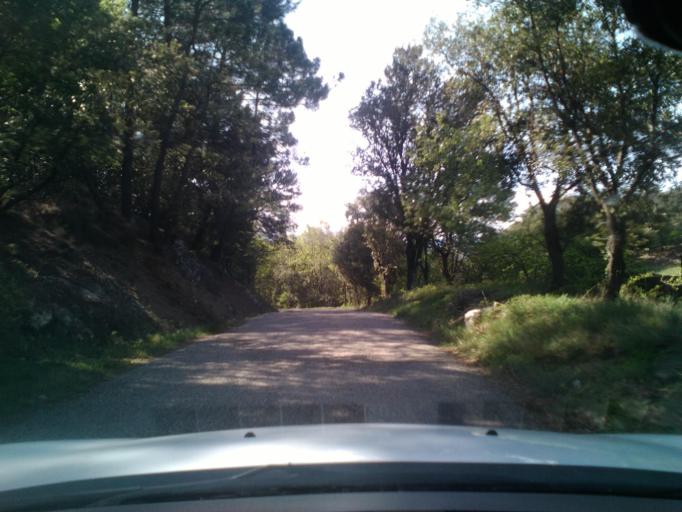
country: FR
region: Languedoc-Roussillon
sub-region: Departement du Gard
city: Lasalle
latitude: 44.0152
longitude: 3.8773
